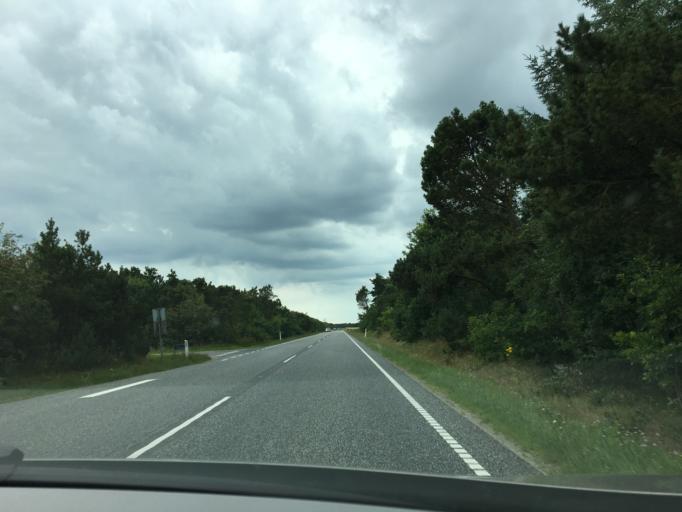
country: DK
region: Central Jutland
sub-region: Ringkobing-Skjern Kommune
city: Skjern
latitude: 55.8675
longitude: 8.3890
